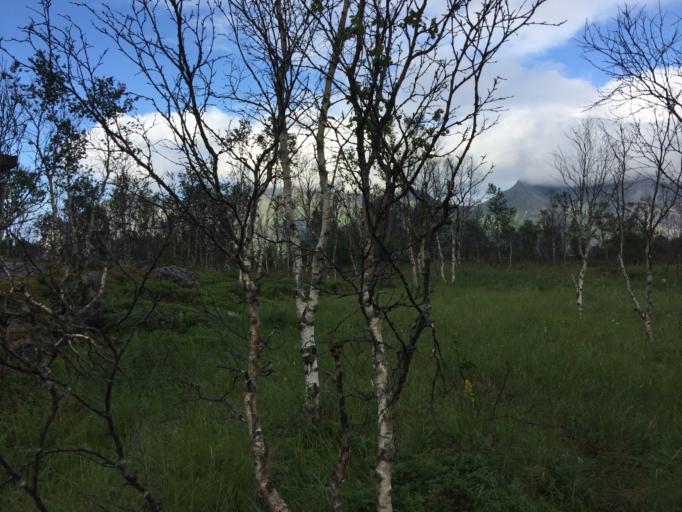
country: NO
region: Troms
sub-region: Berg
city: Skaland
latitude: 69.5120
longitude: 17.4335
